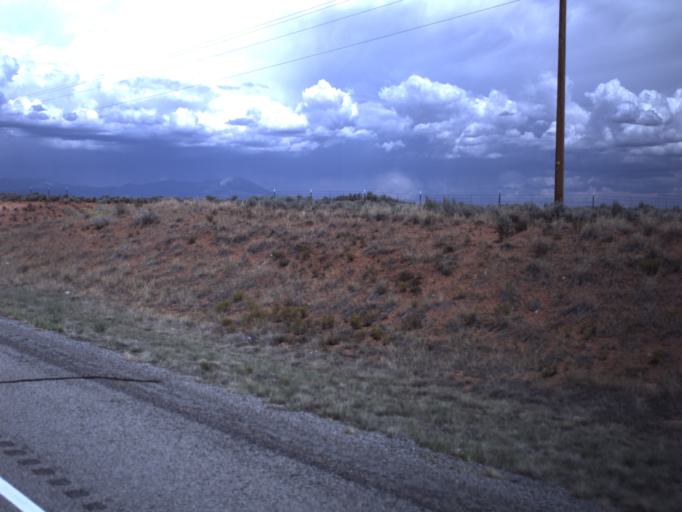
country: US
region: Utah
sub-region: San Juan County
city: Blanding
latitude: 37.5005
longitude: -109.4855
